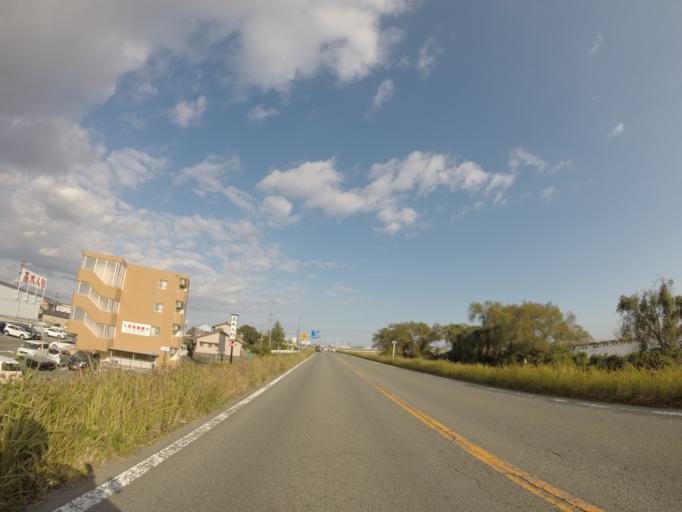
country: JP
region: Shizuoka
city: Shimada
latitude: 34.8284
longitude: 138.2043
